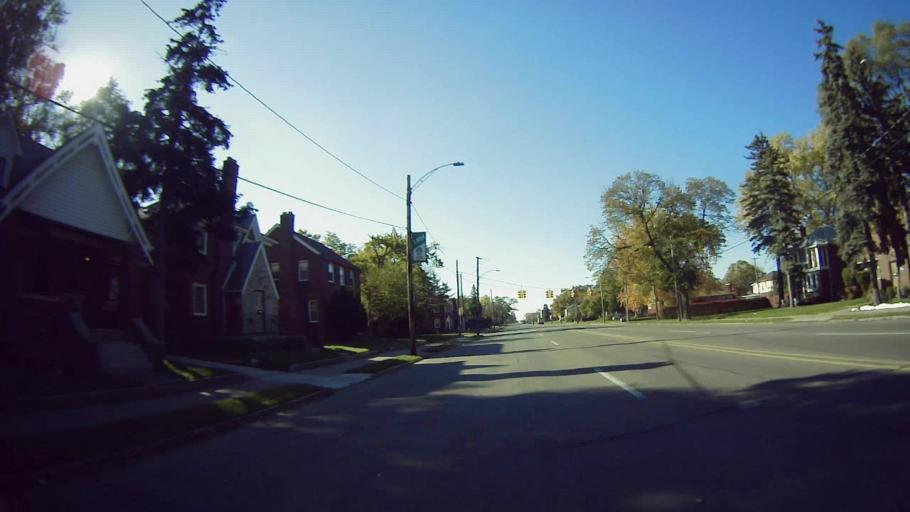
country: US
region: Michigan
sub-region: Oakland County
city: Ferndale
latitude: 42.4314
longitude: -83.1474
